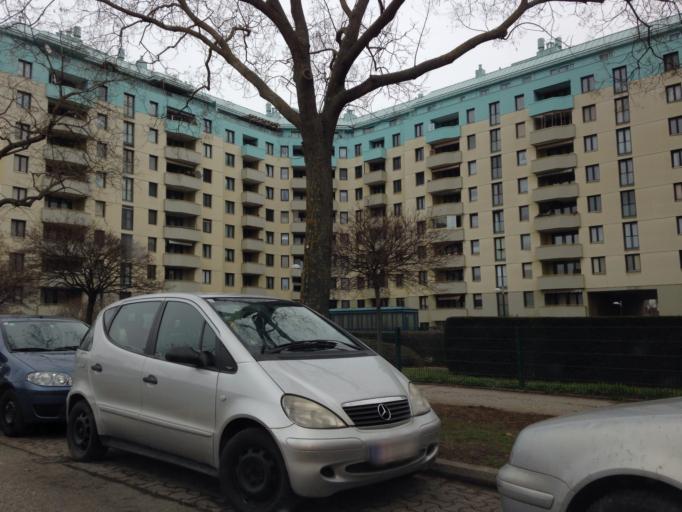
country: AT
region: Lower Austria
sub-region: Politischer Bezirk Wien-Umgebung
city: Gerasdorf bei Wien
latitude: 48.2538
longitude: 16.4527
